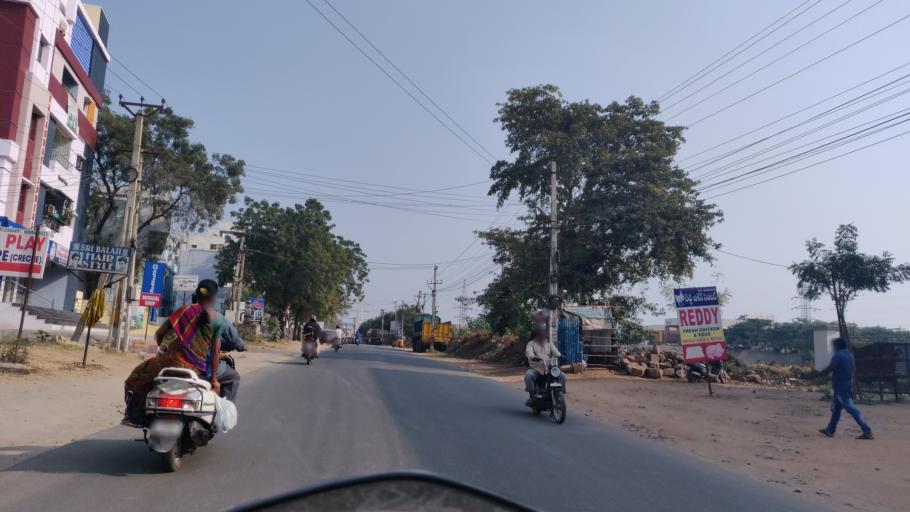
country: IN
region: Telangana
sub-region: Rangareddi
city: Uppal Kalan
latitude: 17.3983
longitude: 78.5866
